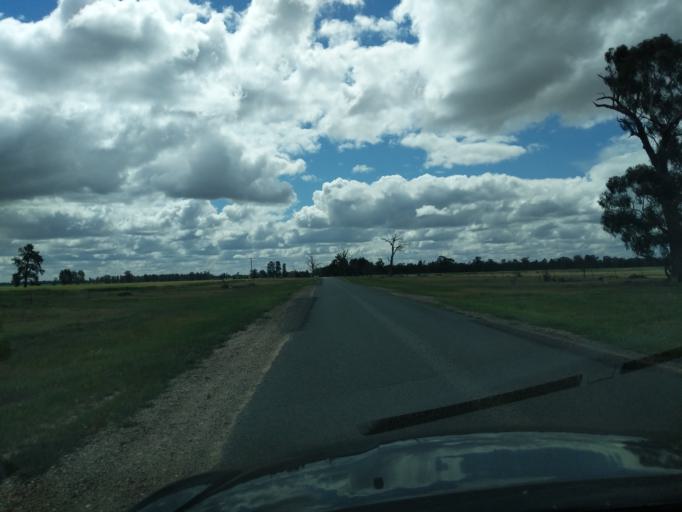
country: AU
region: New South Wales
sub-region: Coolamon
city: Coolamon
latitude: -34.8598
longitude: 146.8980
